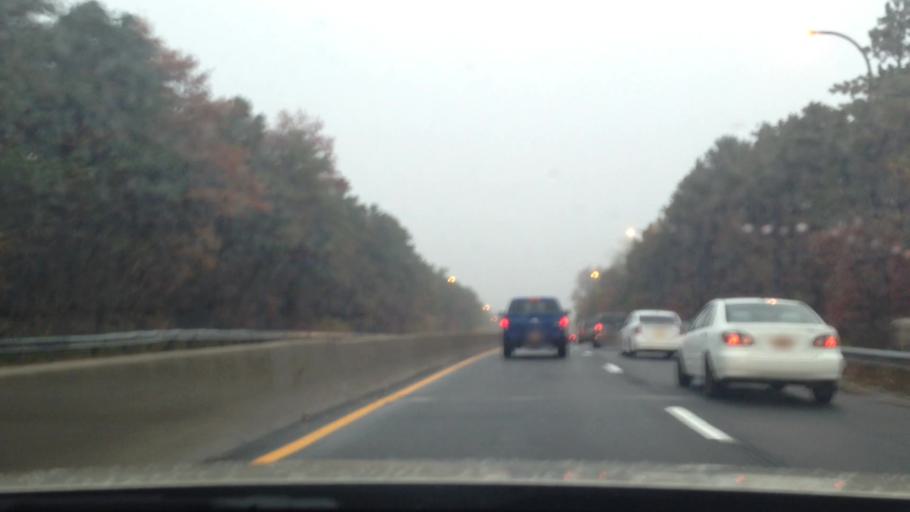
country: US
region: New York
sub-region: Suffolk County
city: Bay Wood
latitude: 40.7726
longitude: -73.2800
